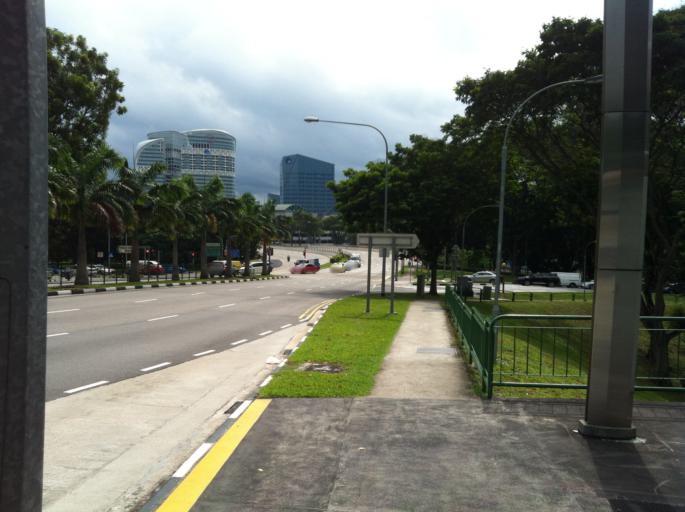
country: SG
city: Singapore
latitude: 1.2929
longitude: 103.7847
